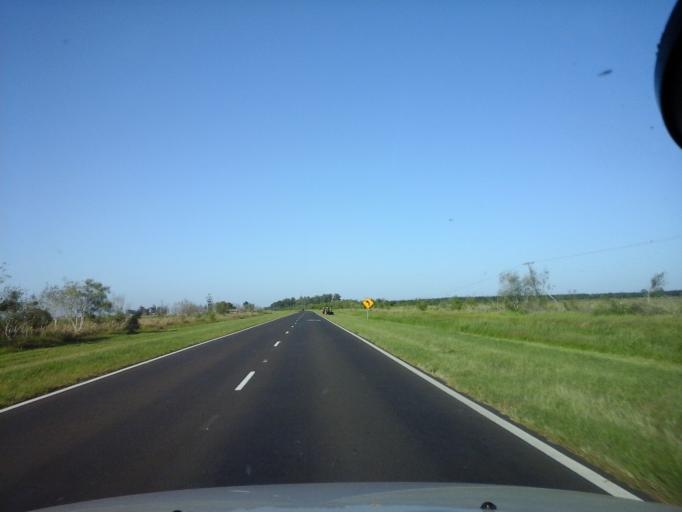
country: AR
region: Corrientes
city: Ita Ibate
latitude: -27.4451
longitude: -57.3863
